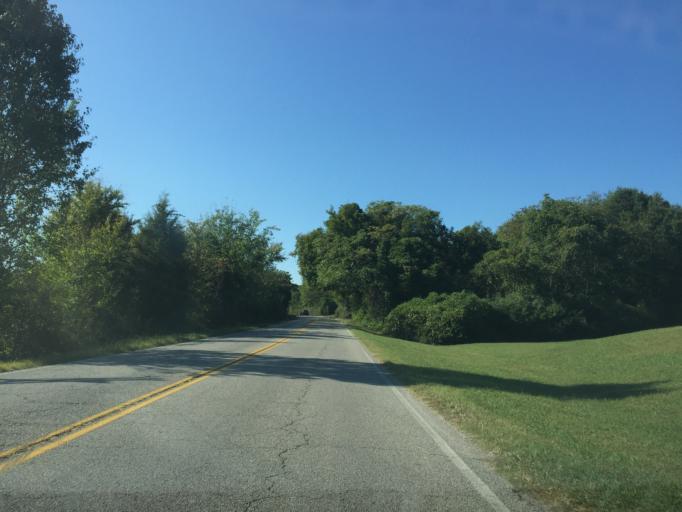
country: US
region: Tennessee
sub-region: Hamilton County
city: Harrison
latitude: 35.1001
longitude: -85.1588
